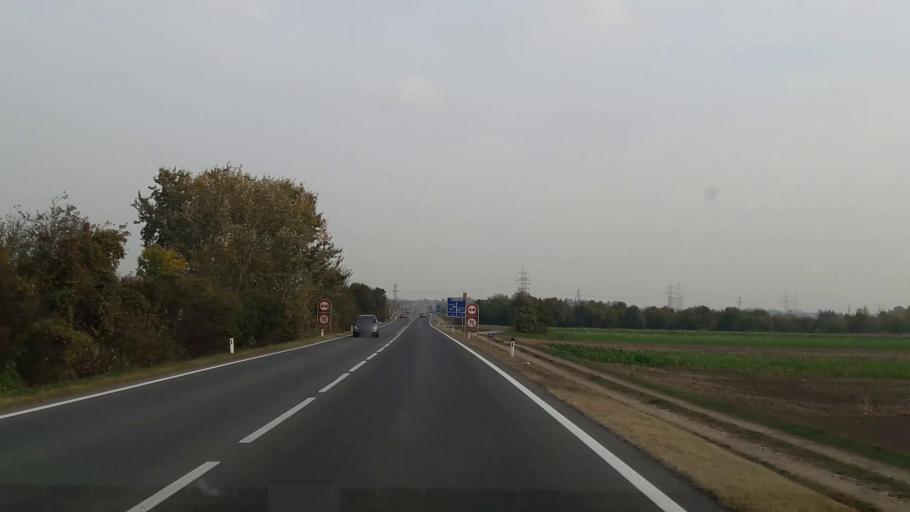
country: AT
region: Burgenland
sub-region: Politischer Bezirk Neusiedl am See
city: Parndorf
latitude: 48.0067
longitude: 16.8288
